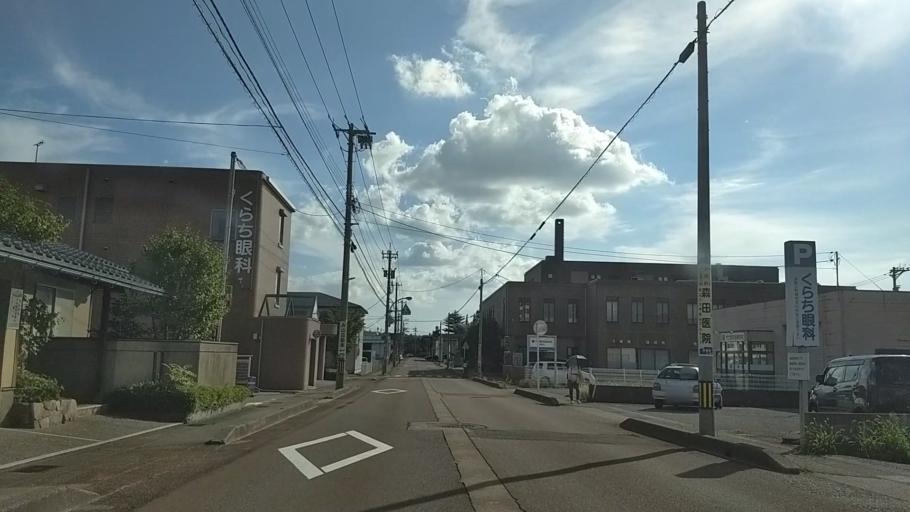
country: JP
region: Ishikawa
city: Kanazawa-shi
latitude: 36.5823
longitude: 136.6677
